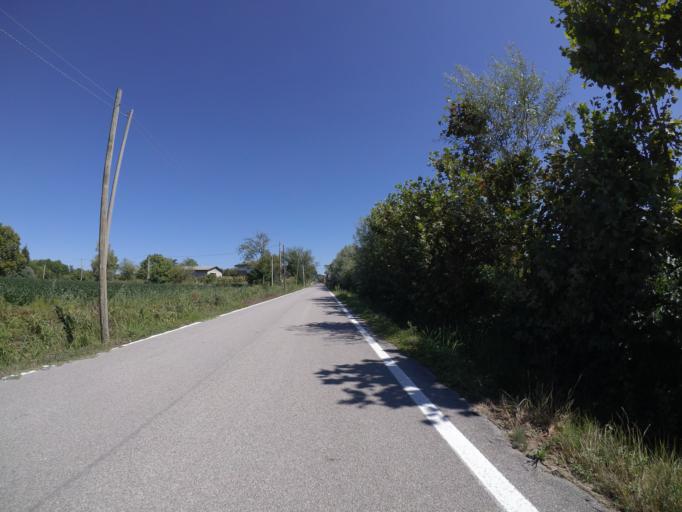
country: IT
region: Friuli Venezia Giulia
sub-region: Provincia di Udine
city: Rivignano
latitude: 45.8734
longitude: 13.0288
